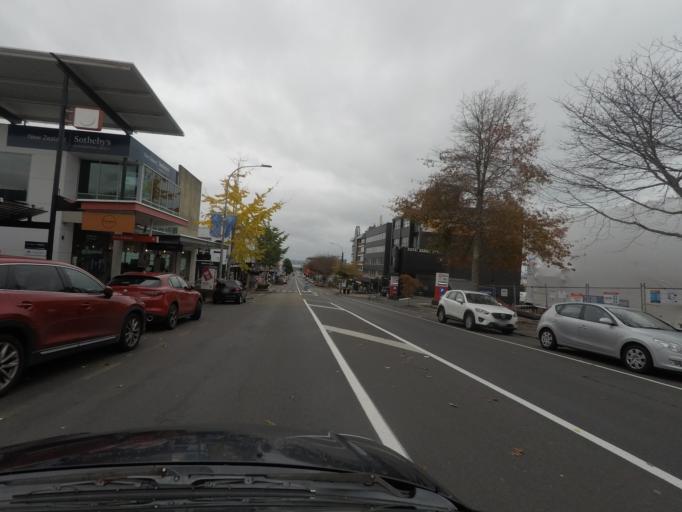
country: NZ
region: Auckland
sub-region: Auckland
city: Auckland
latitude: -36.8568
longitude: 174.7814
